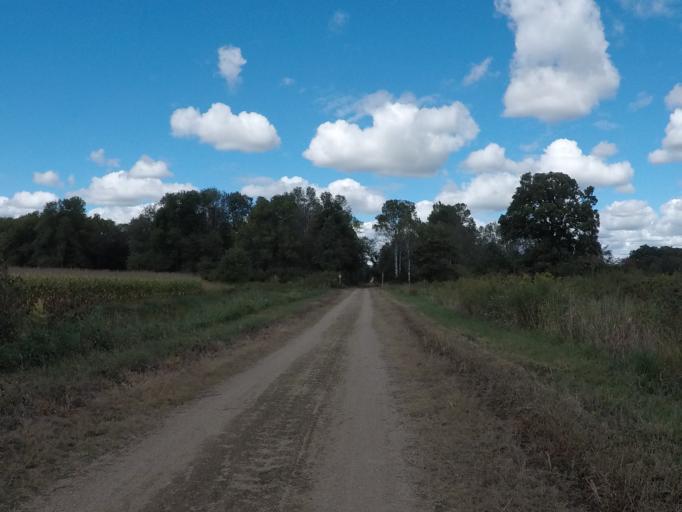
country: US
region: Wisconsin
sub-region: Richland County
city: Richland Center
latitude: 43.3000
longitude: -90.3351
